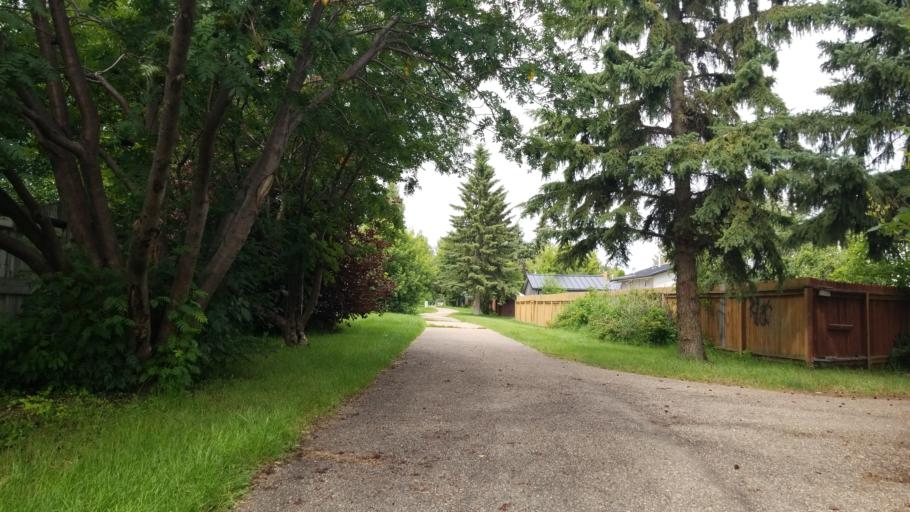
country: CA
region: Saskatchewan
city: Lloydminster
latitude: 53.2634
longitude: -110.0176
